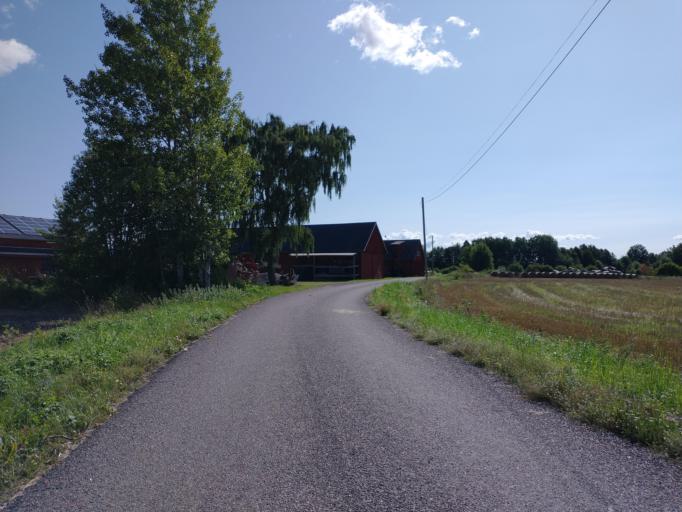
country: SE
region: Kalmar
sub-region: Kalmar Kommun
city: Lindsdal
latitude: 56.7946
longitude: 16.2785
